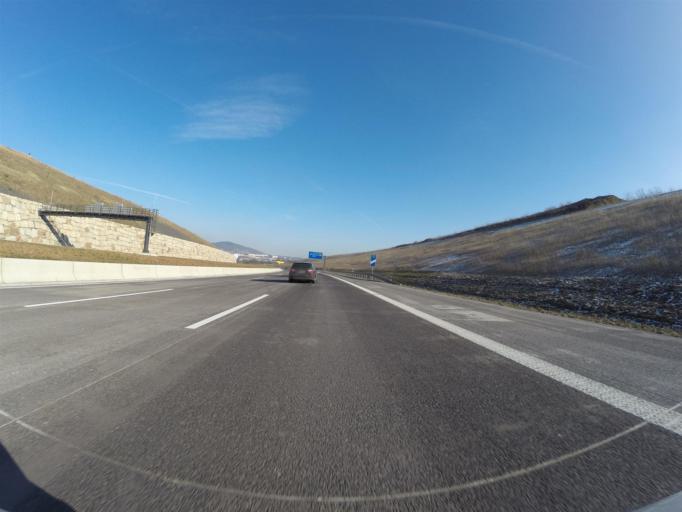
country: DE
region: Thuringia
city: Rothenstein
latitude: 50.8704
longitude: 11.5888
